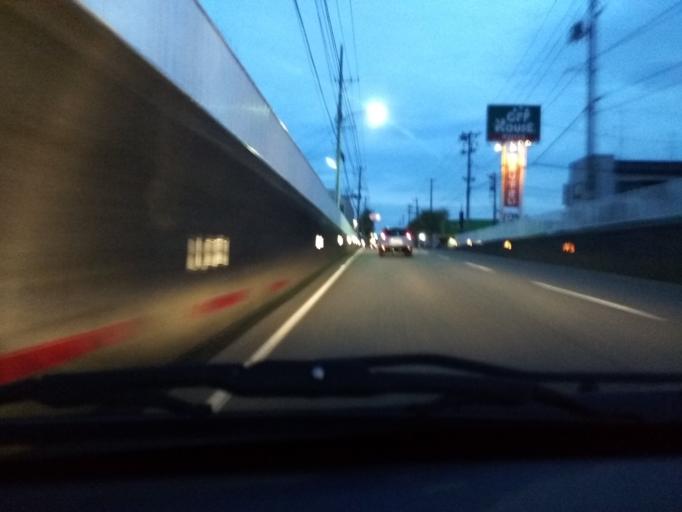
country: JP
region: Niigata
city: Kashiwazaki
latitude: 37.3689
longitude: 138.5644
